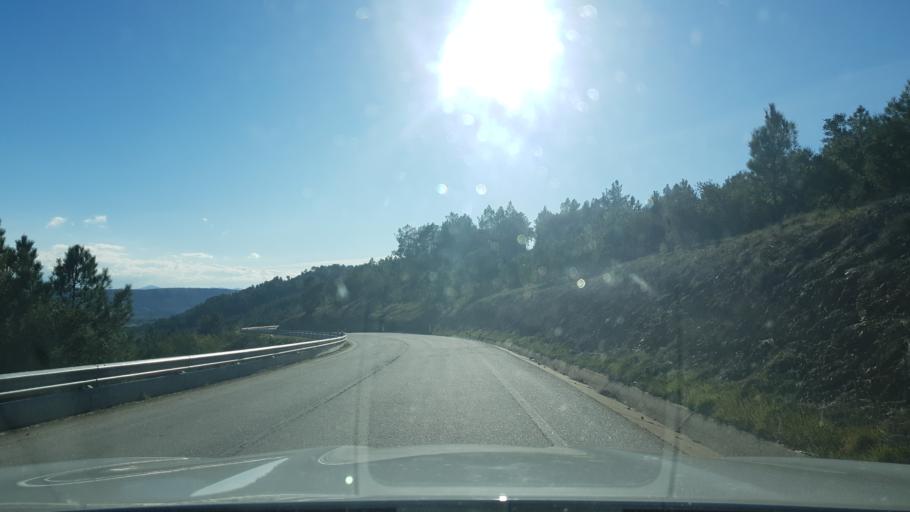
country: PT
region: Braganca
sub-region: Freixo de Espada A Cinta
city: Freixo de Espada a Cinta
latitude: 41.1110
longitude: -6.8230
